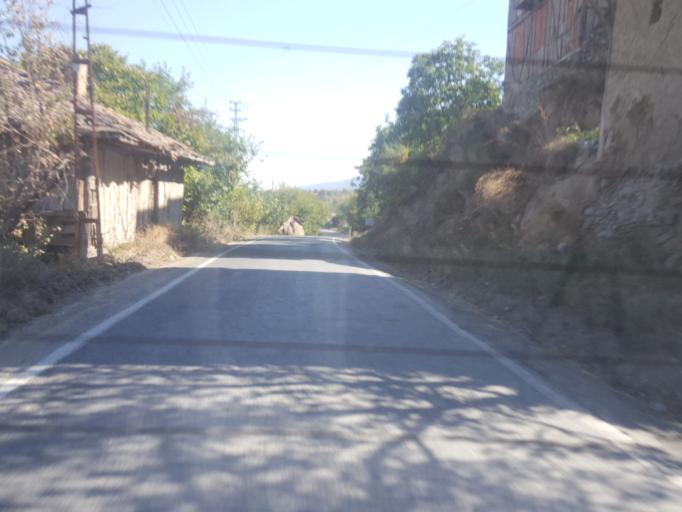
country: TR
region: Kastamonu
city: Tosya
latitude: 40.9869
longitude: 34.1066
